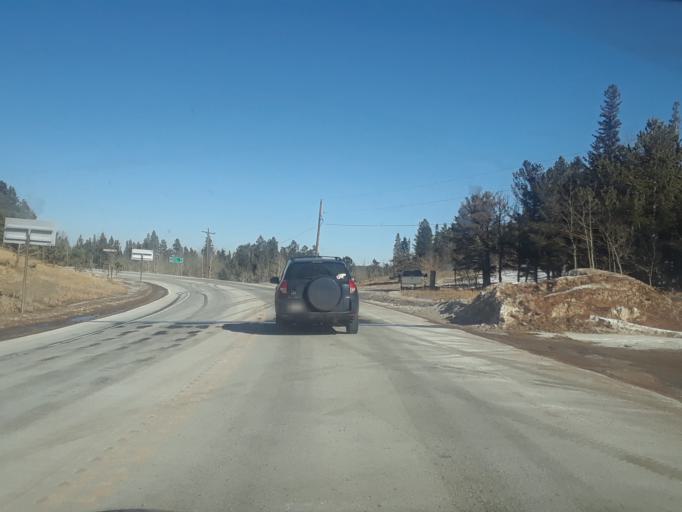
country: US
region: Colorado
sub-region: Boulder County
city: Nederland
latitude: 40.0753
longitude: -105.5040
